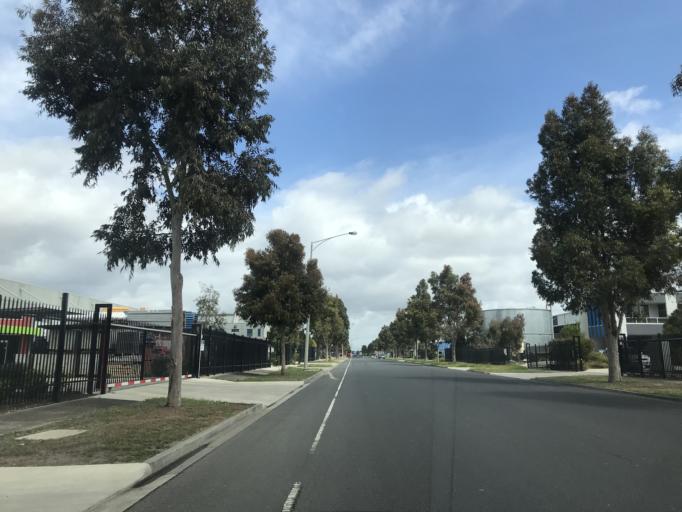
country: AU
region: Victoria
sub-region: Brimbank
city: Derrimut
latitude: -37.7887
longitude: 144.7840
